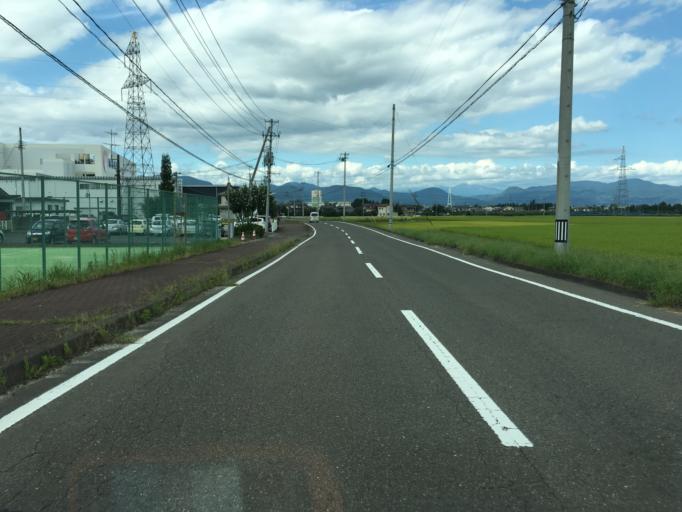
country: JP
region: Fukushima
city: Fukushima-shi
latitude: 37.7393
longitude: 140.4079
